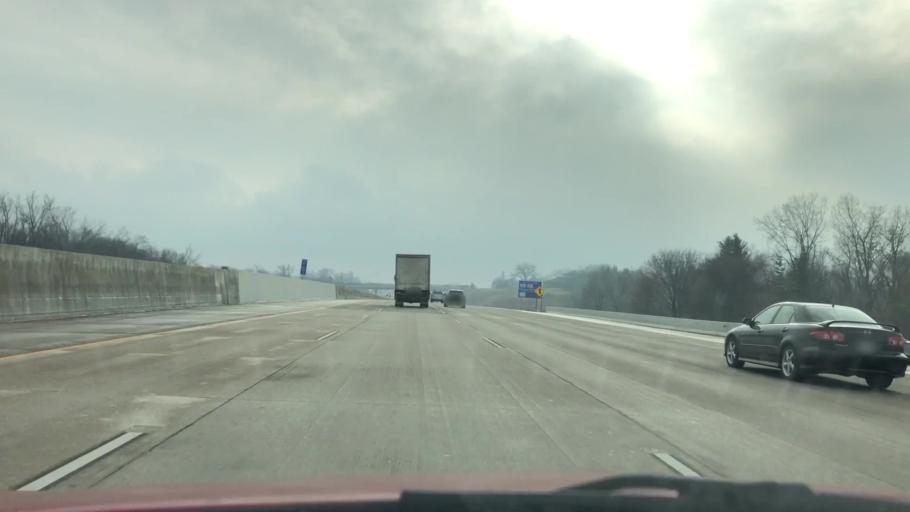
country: US
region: Wisconsin
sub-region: Brown County
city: Ashwaubenon
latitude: 44.4841
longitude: -88.0806
